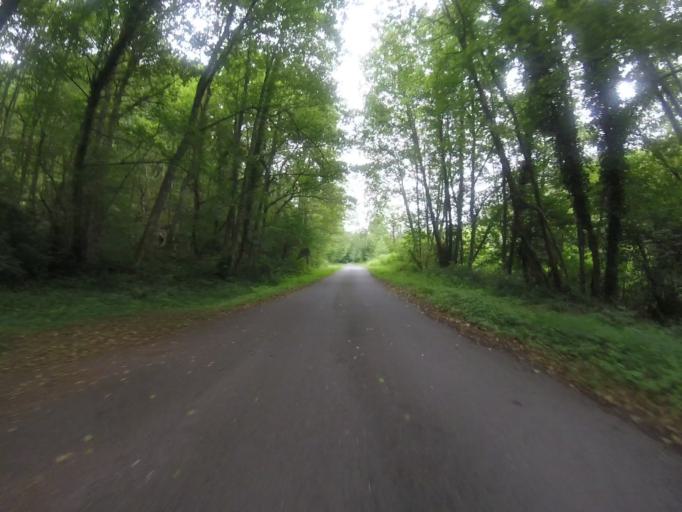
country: ES
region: Navarre
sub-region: Provincia de Navarra
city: Areso
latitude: 43.1055
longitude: -1.9377
